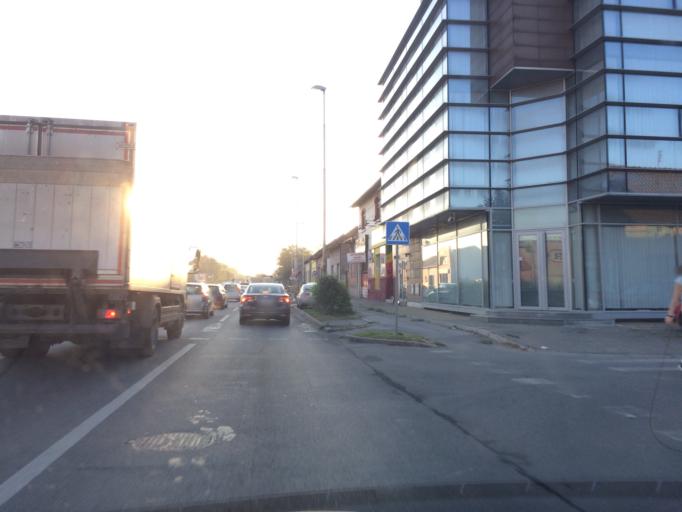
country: RS
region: Autonomna Pokrajina Vojvodina
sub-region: Juznobacki Okrug
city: Novi Sad
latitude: 45.2700
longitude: 19.8398
